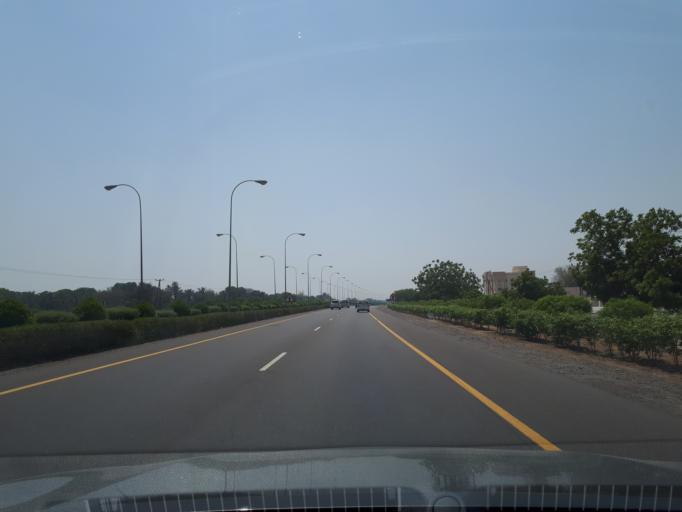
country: OM
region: Al Batinah
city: Al Sohar
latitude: 24.3959
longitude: 56.6756
